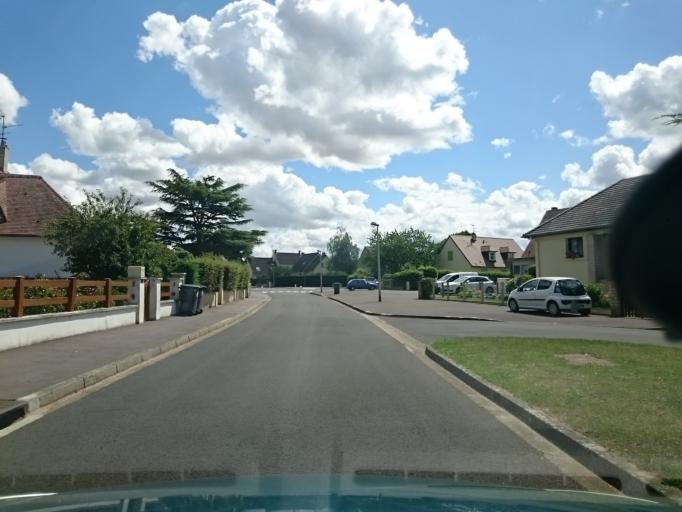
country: FR
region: Lower Normandy
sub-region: Departement du Calvados
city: Ifs
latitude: 49.1441
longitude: -0.3548
